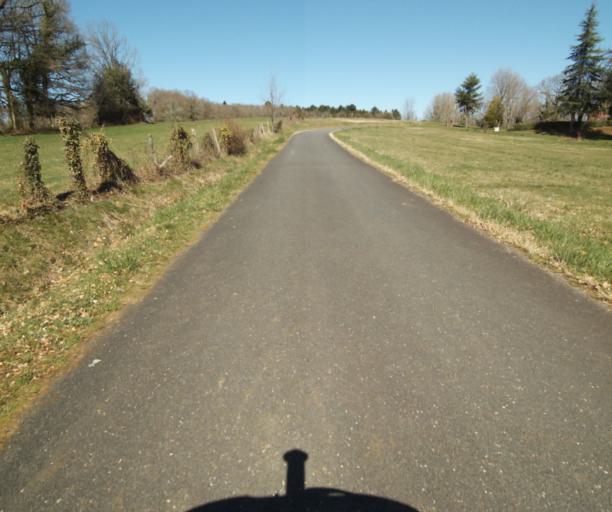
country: FR
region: Limousin
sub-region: Departement de la Correze
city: Seilhac
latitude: 45.3765
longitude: 1.6926
